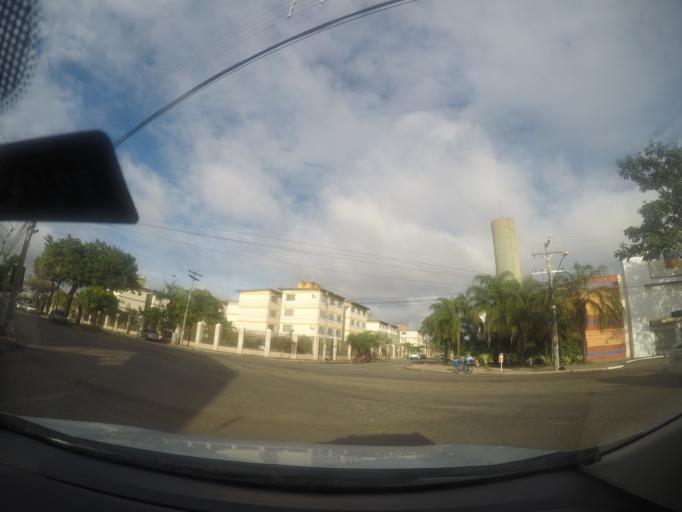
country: BR
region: Goias
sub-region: Goiania
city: Goiania
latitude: -16.6834
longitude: -49.3132
